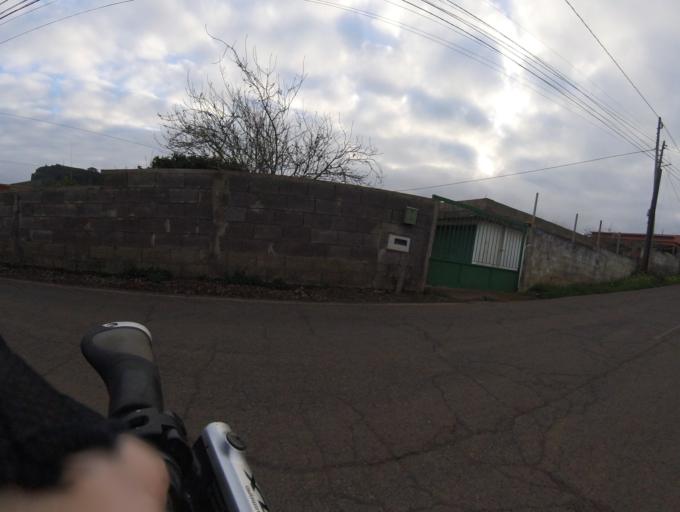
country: ES
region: Canary Islands
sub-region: Provincia de Santa Cruz de Tenerife
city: La Laguna
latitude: 28.4507
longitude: -16.3553
